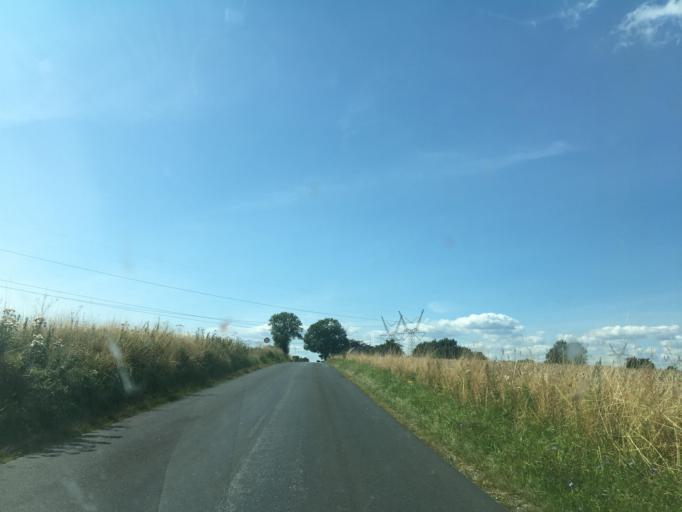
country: DK
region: South Denmark
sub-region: Middelfart Kommune
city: Ejby
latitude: 55.4265
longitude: 9.9080
